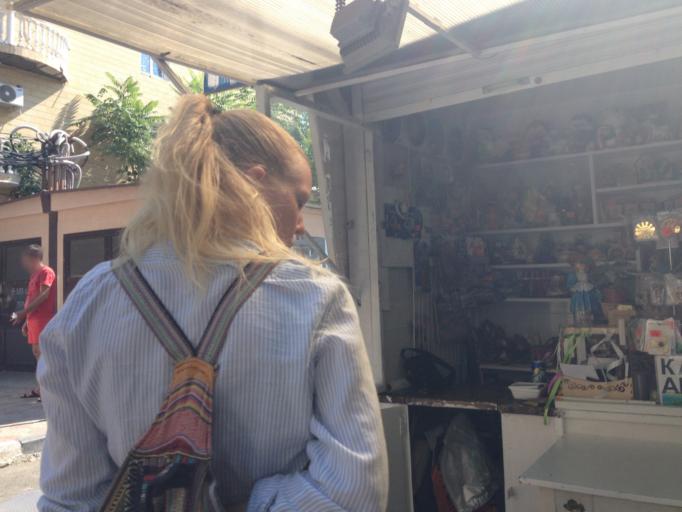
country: RU
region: Krasnodarskiy
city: Anapa
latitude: 44.8928
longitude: 37.3128
